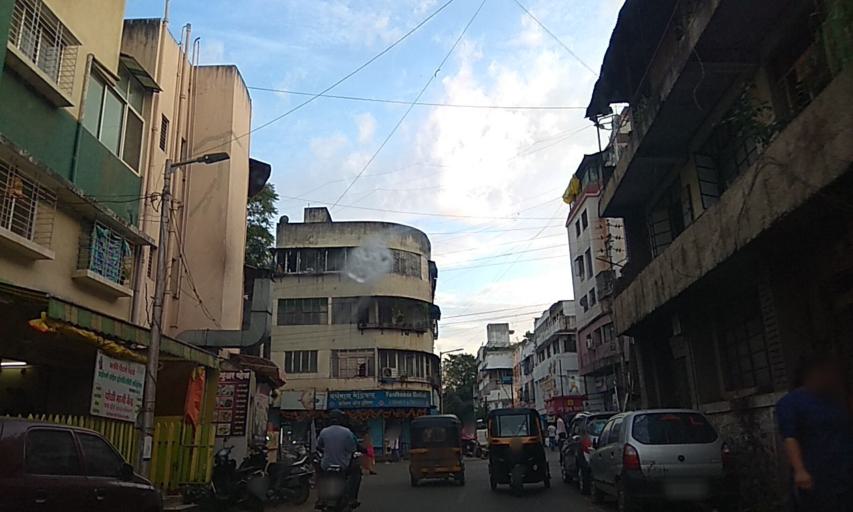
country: IN
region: Maharashtra
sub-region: Pune Division
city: Pune
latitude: 18.4977
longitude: 73.8511
